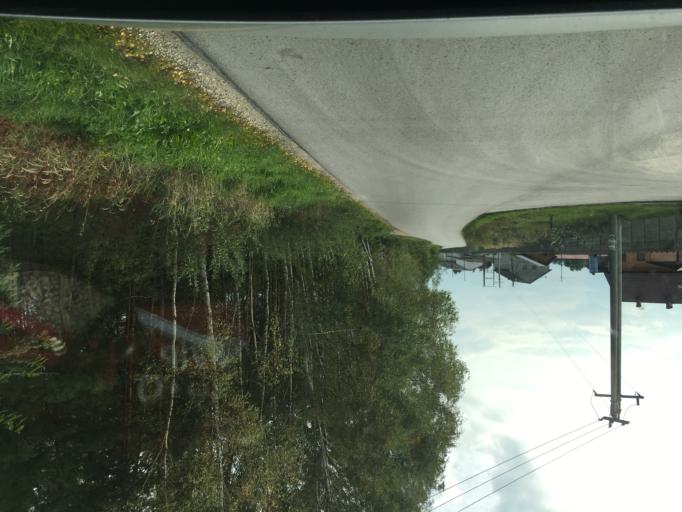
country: PL
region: Swietokrzyskie
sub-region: Powiat pinczowski
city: Michalow
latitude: 50.5023
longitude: 20.4844
